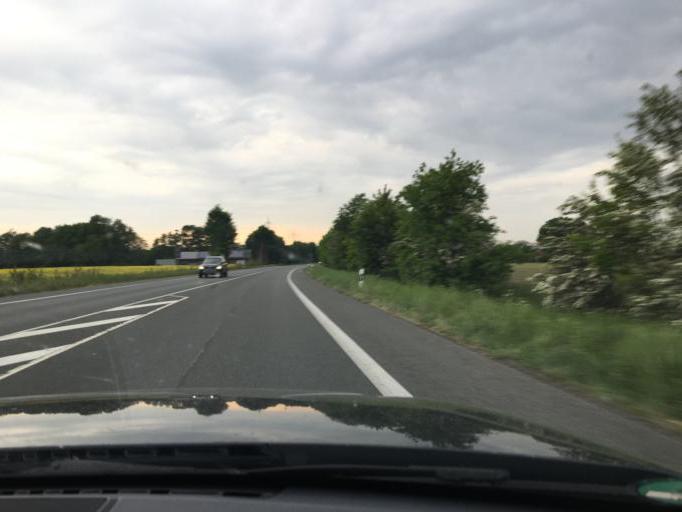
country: DE
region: North Rhine-Westphalia
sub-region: Regierungsbezirk Munster
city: Greven
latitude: 52.1284
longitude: 7.5809
